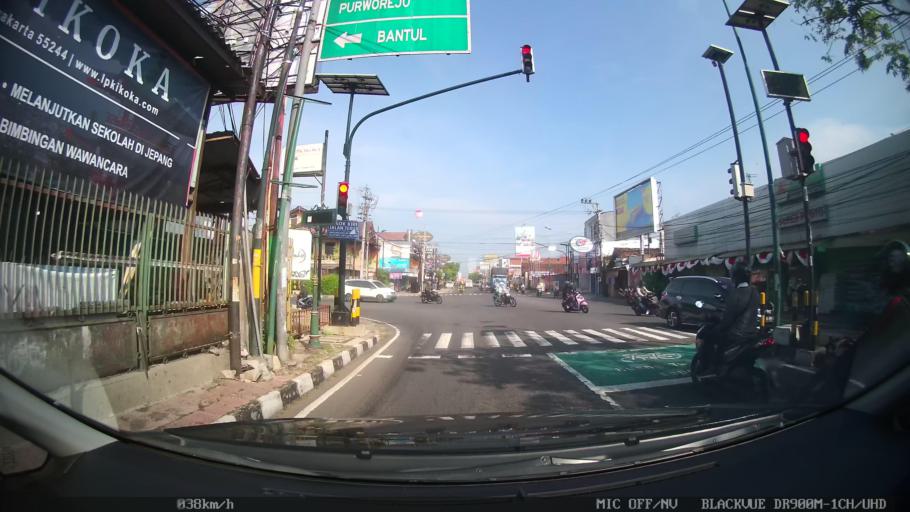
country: ID
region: Daerah Istimewa Yogyakarta
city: Yogyakarta
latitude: -7.7818
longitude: 110.3531
